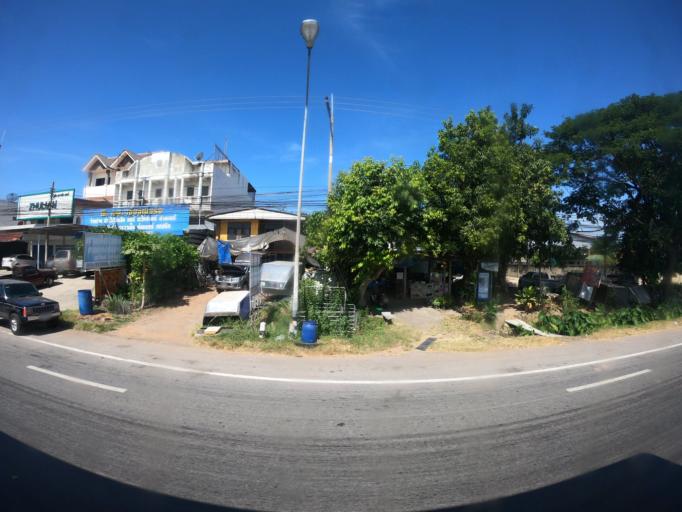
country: TH
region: Nakhon Ratchasima
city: Nakhon Ratchasima
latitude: 15.0326
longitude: 102.1421
